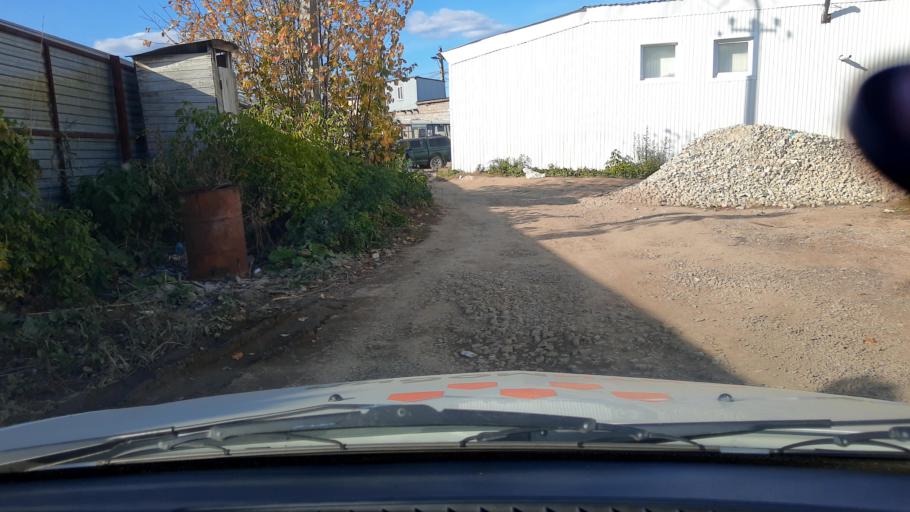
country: RU
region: Bashkortostan
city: Ufa
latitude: 54.7947
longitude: 56.0928
